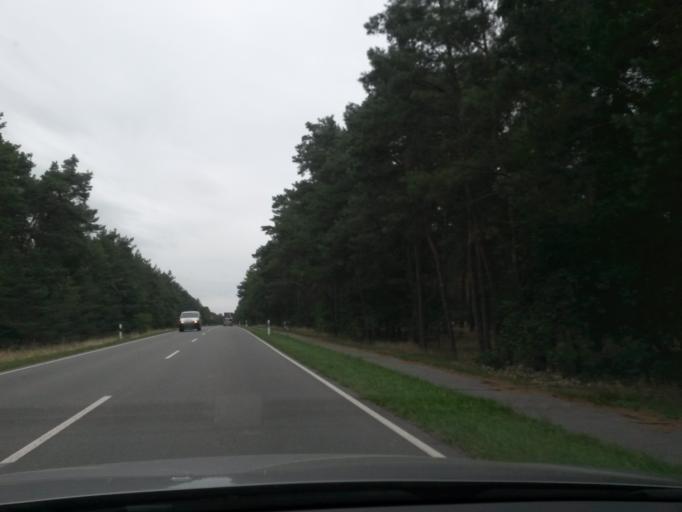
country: DE
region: Saxony-Anhalt
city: Klietz
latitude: 52.6777
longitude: 12.0639
